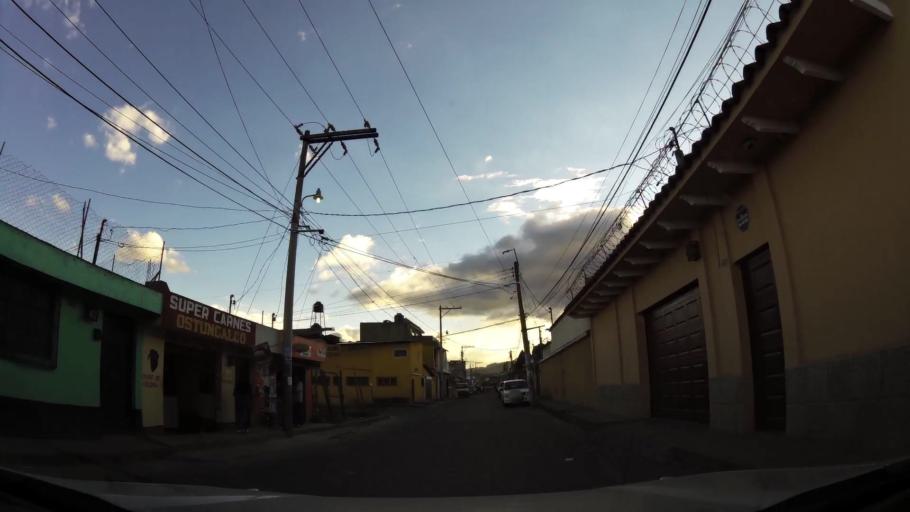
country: GT
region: Quetzaltenango
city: Quetzaltenango
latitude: 14.8557
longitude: -91.5332
